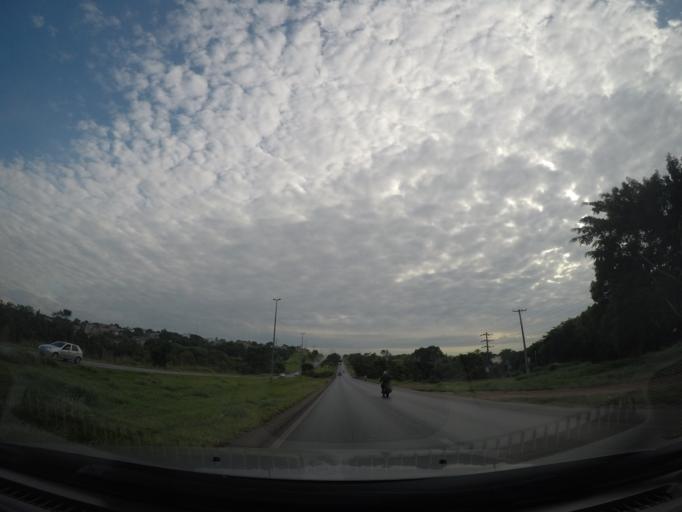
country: BR
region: Goias
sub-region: Planaltina
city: Planaltina
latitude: -15.6077
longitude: -47.6926
